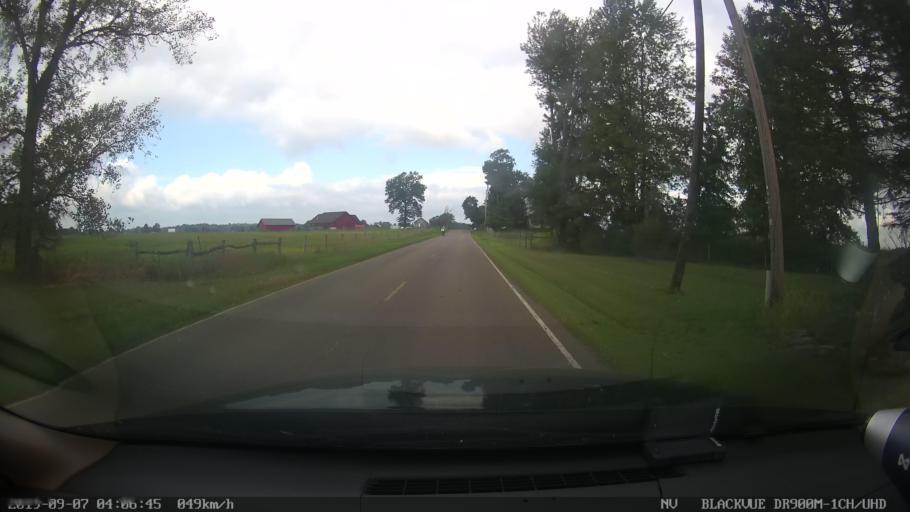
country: US
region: Ohio
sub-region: Licking County
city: Johnstown
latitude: 40.2012
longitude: -82.6077
